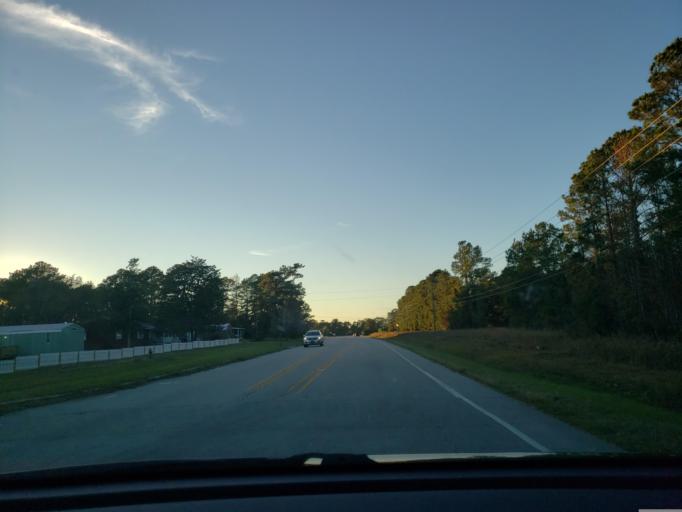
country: US
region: North Carolina
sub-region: Onslow County
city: Sneads Ferry
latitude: 34.5885
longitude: -77.4735
